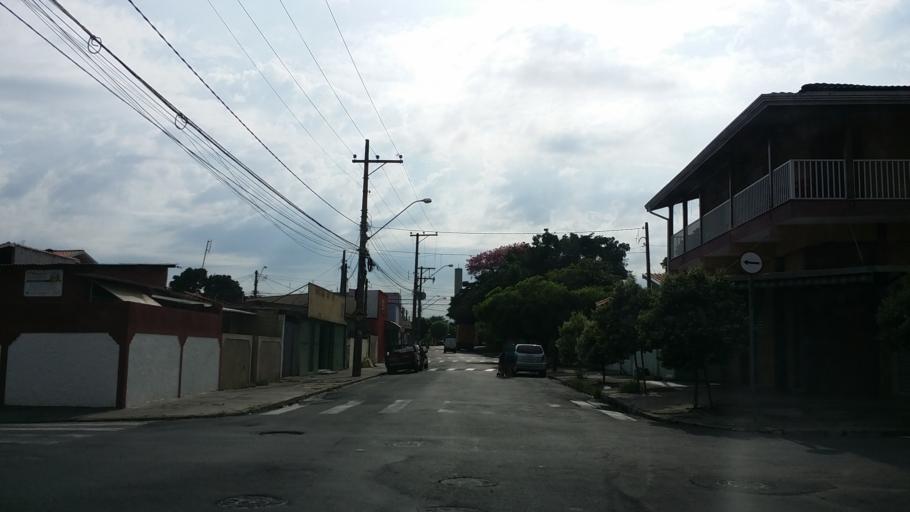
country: BR
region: Sao Paulo
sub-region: Indaiatuba
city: Indaiatuba
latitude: -23.1040
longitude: -47.2147
